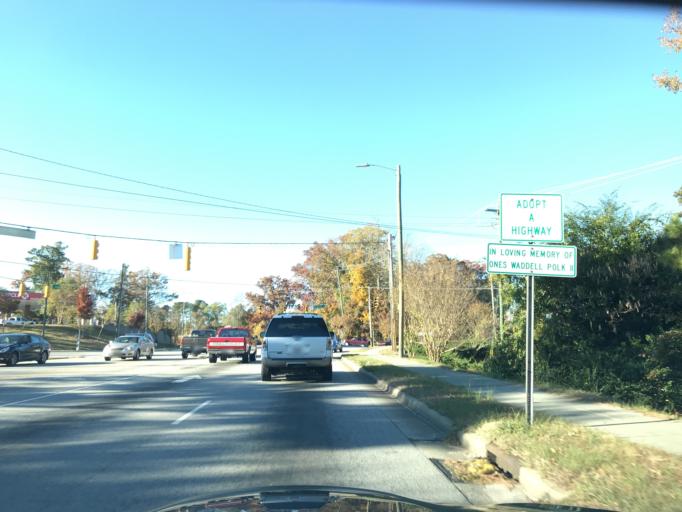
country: US
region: North Carolina
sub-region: Wake County
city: Raleigh
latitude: 35.7706
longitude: -78.5827
